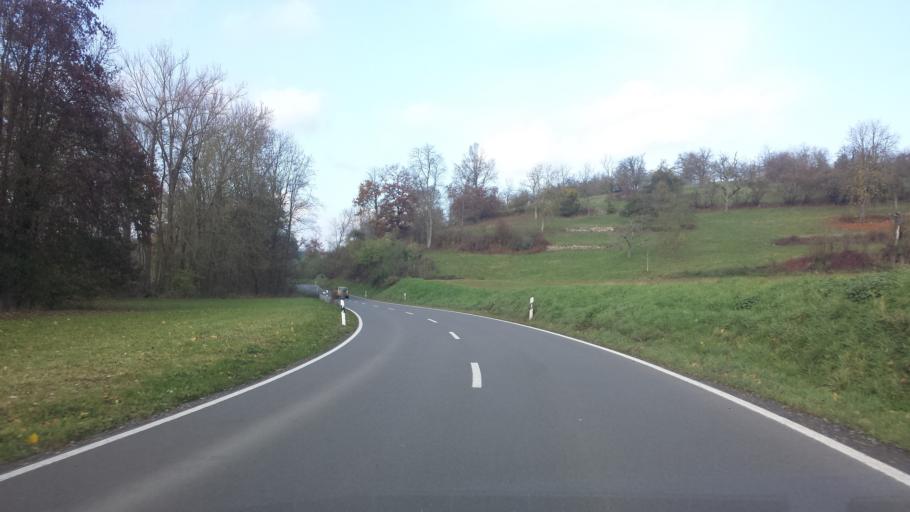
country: DE
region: Baden-Wuerttemberg
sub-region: Karlsruhe Region
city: Zaisenhausen
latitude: 49.1160
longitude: 8.7436
